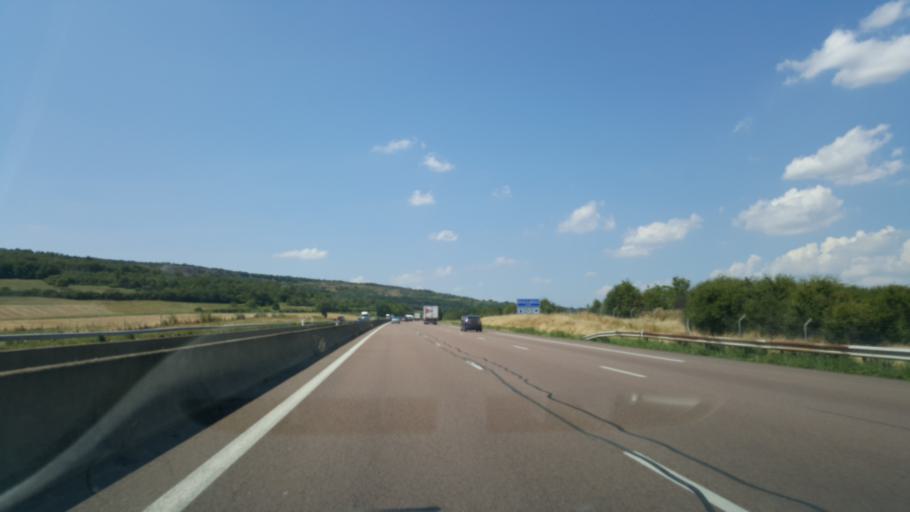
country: FR
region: Bourgogne
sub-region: Departement de Saone-et-Loire
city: Sennecey-le-Grand
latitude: 46.6113
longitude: 4.8734
